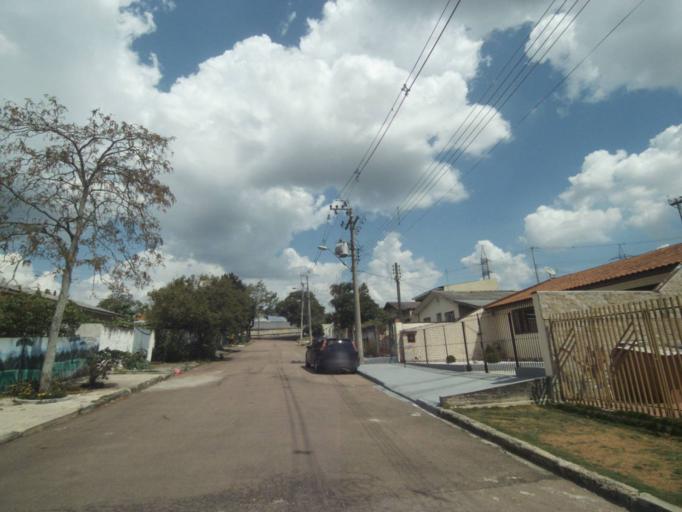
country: BR
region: Parana
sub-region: Sao Jose Dos Pinhais
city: Sao Jose dos Pinhais
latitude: -25.5360
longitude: -49.2786
